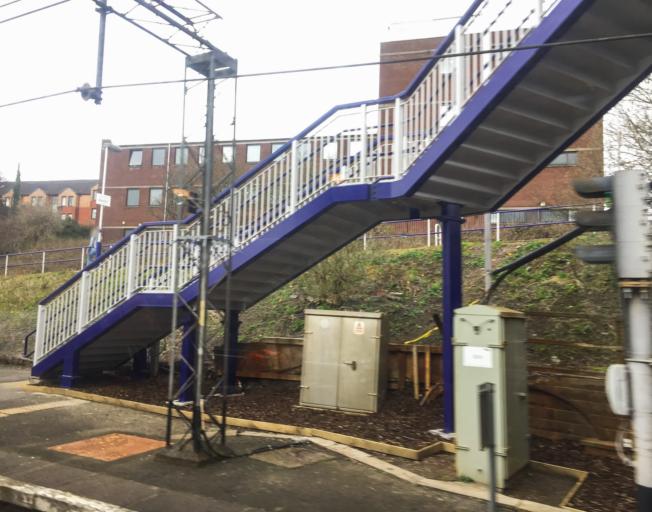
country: GB
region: Scotland
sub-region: West Dunbartonshire
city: Clydebank
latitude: 55.9071
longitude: -4.4042
